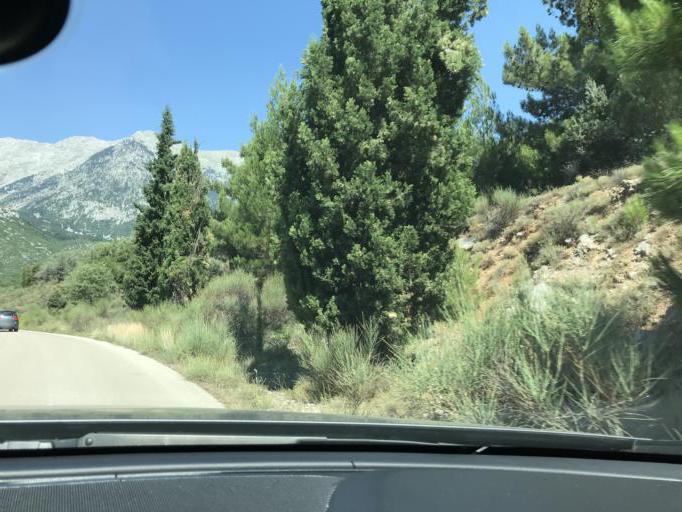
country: GR
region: Central Greece
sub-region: Nomos Voiotias
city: Distomo
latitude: 38.5104
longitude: 22.7166
